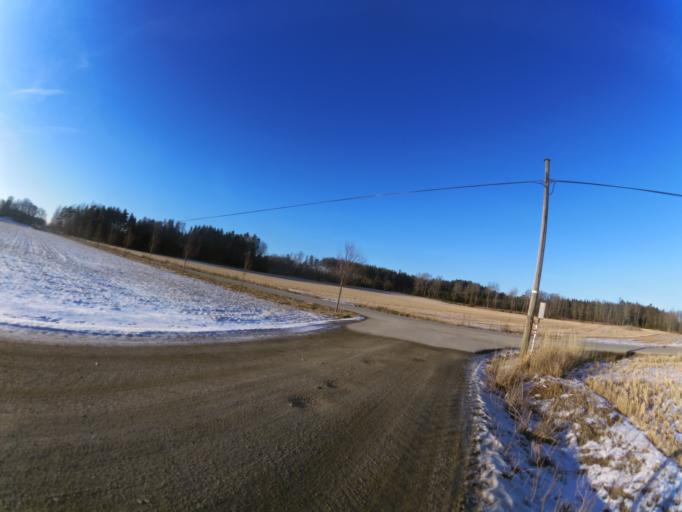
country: NO
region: Ostfold
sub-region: Fredrikstad
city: Lervik
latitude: 59.2527
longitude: 10.8099
